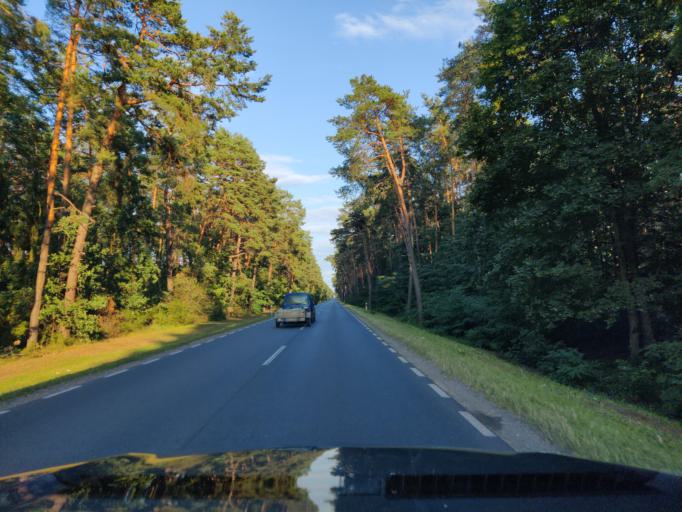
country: PL
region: Masovian Voivodeship
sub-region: Powiat pultuski
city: Pultusk
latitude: 52.6788
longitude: 21.1379
